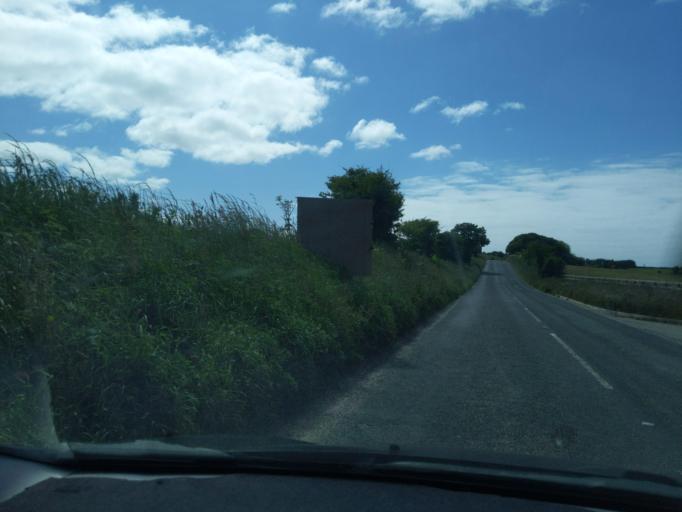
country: GB
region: England
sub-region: Cornwall
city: Perranporth
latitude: 50.2972
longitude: -5.1329
